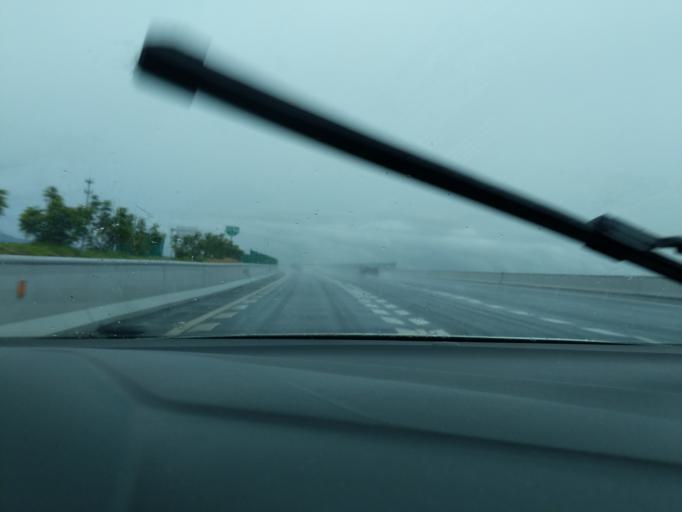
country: CN
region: Guangdong
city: Zhishan
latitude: 22.4863
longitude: 112.7946
